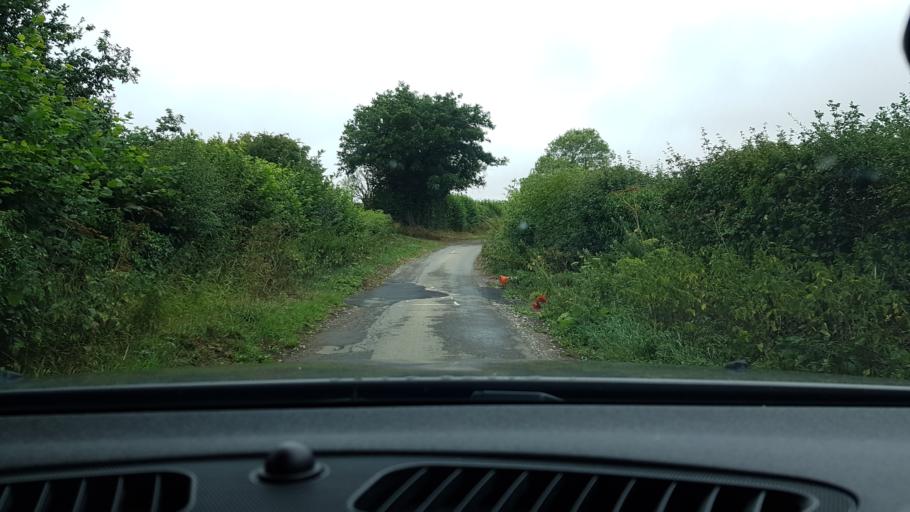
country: GB
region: England
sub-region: Wiltshire
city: Shalbourne
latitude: 51.3347
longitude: -1.5107
